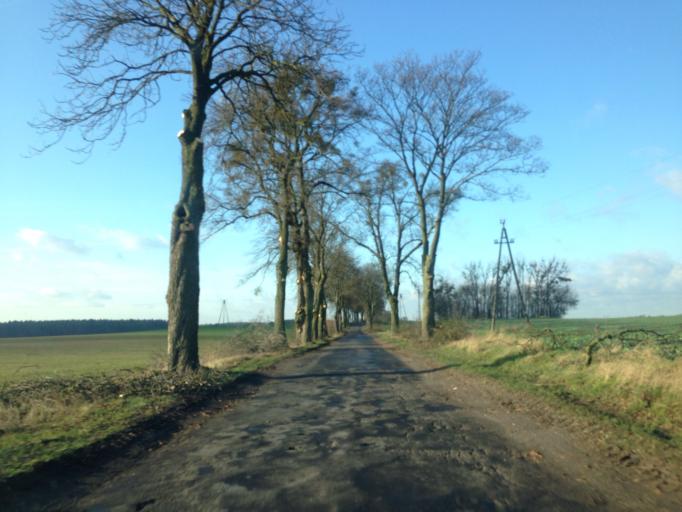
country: PL
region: Kujawsko-Pomorskie
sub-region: Powiat grudziadzki
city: Swiecie nad Osa
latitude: 53.4658
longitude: 19.1363
